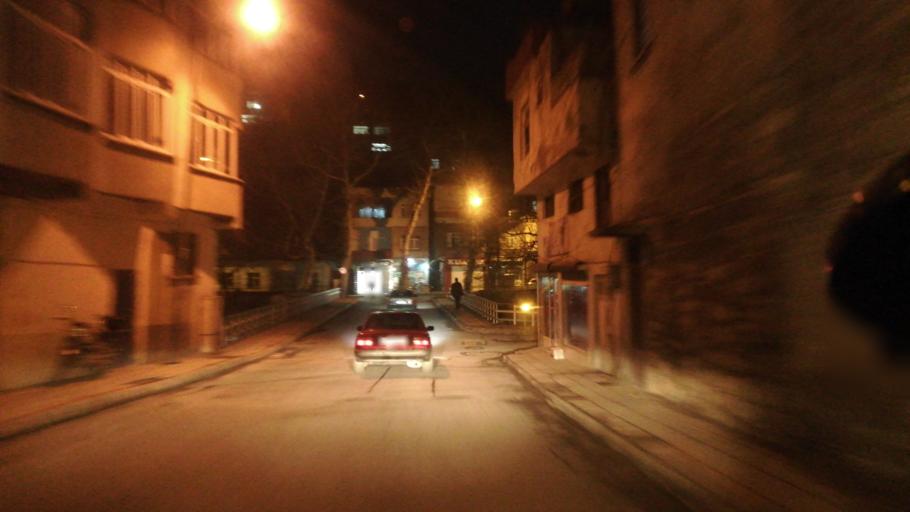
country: TR
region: Kahramanmaras
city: Kahramanmaras
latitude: 37.5859
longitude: 36.9291
